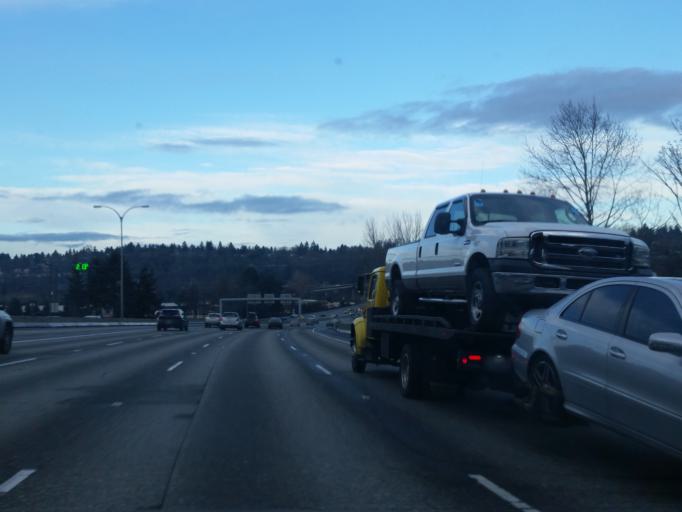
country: US
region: Washington
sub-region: King County
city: Tukwila
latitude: 47.4824
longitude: -122.2710
